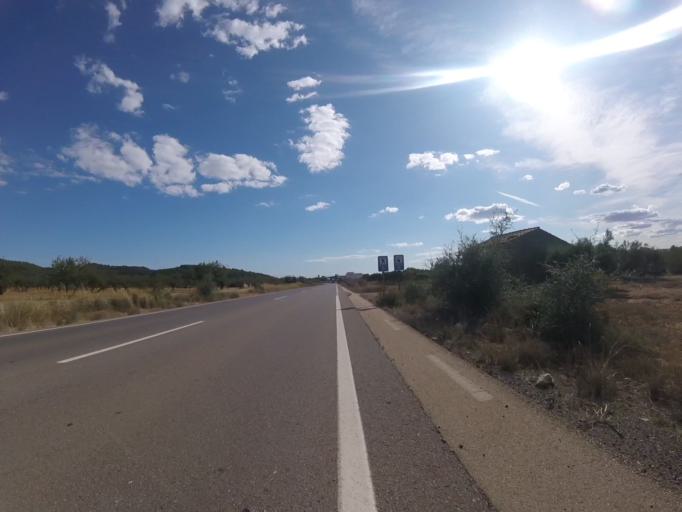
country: ES
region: Valencia
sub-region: Provincia de Castello
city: Alcoceber
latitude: 40.2598
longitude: 0.2438
